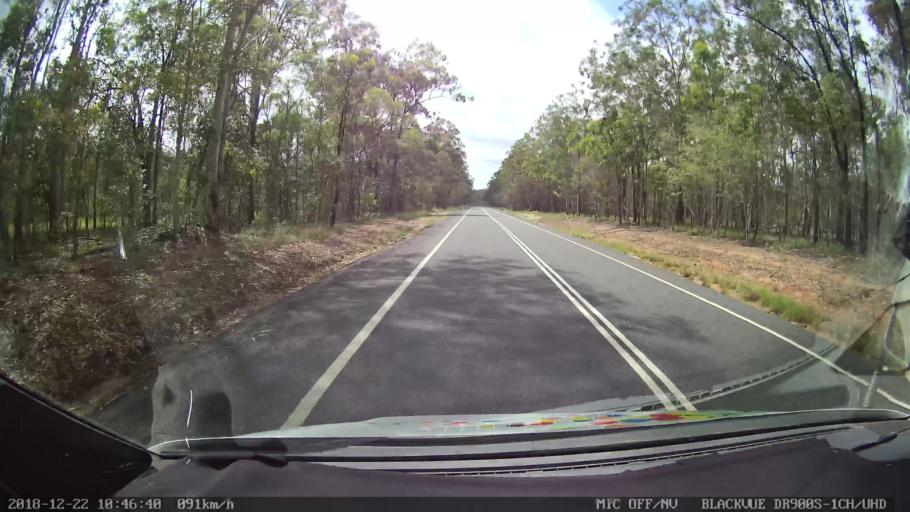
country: AU
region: New South Wales
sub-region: Clarence Valley
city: South Grafton
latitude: -29.6676
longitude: 152.8285
